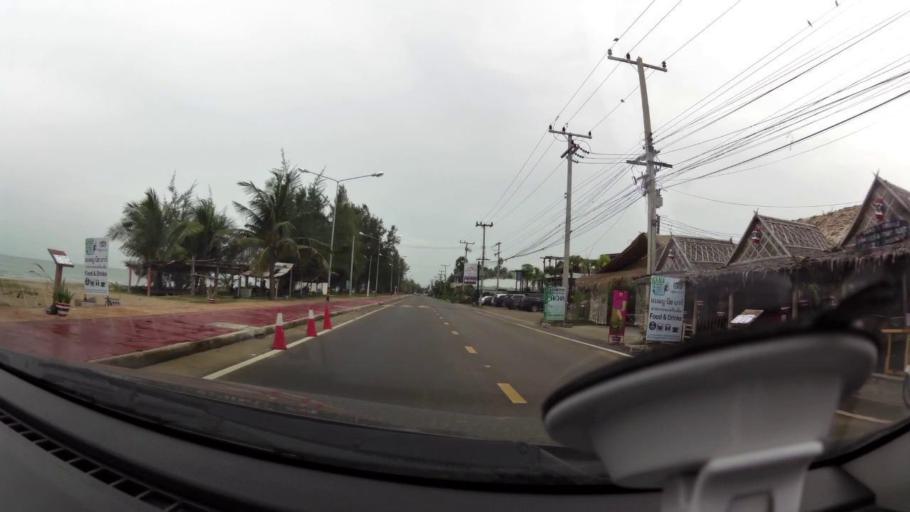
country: TH
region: Prachuap Khiri Khan
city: Pran Buri
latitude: 12.3685
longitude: 99.9998
